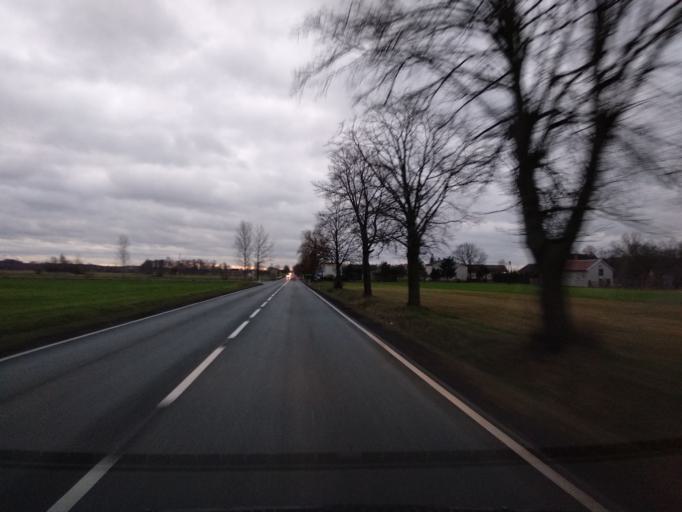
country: PL
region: Greater Poland Voivodeship
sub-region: Powiat koninski
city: Stare Miasto
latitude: 52.1406
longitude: 18.1916
